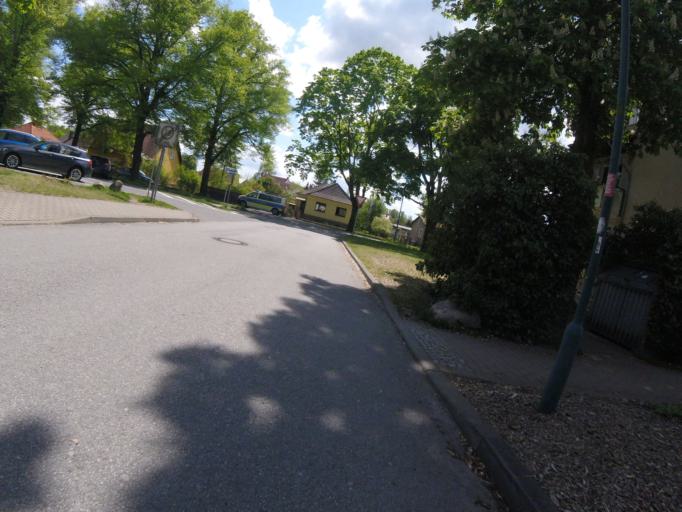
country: DE
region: Brandenburg
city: Konigs Wusterhausen
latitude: 52.2984
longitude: 13.6165
